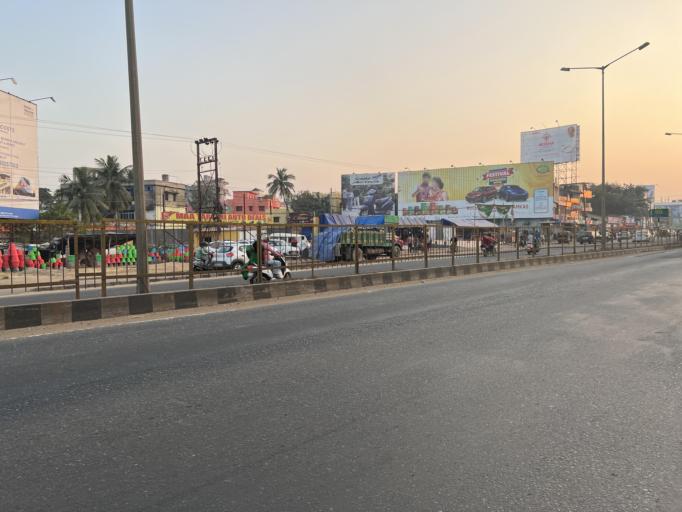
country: IN
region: Odisha
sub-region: Khordha
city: Bhubaneshwar
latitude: 20.3026
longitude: 85.8654
